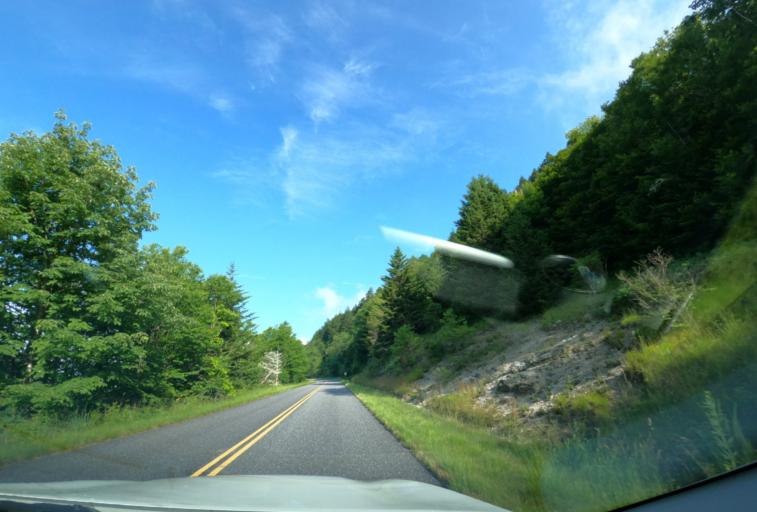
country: US
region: North Carolina
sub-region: Haywood County
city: Hazelwood
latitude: 35.2998
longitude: -82.9270
